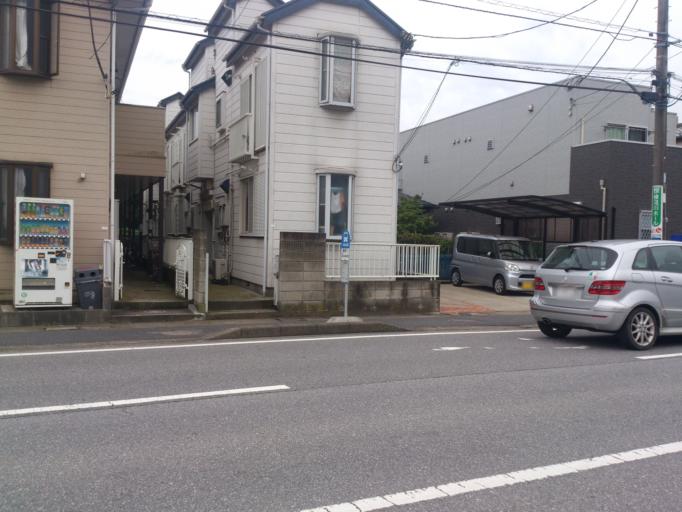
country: JP
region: Chiba
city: Chiba
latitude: 35.6457
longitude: 140.0687
